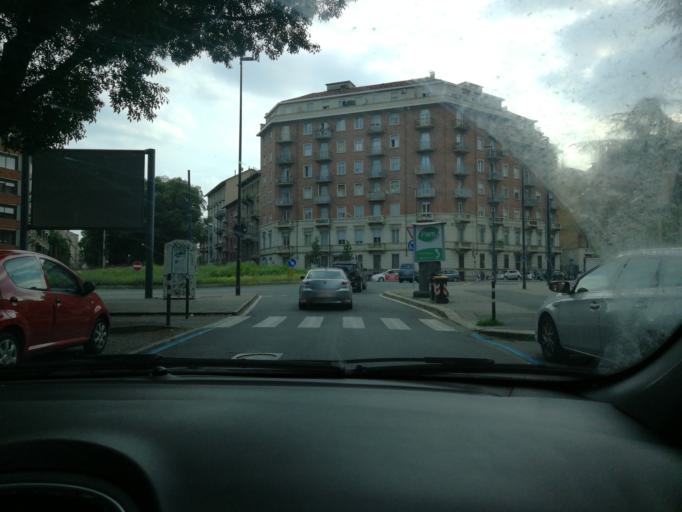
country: IT
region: Piedmont
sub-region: Provincia di Torino
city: Turin
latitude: 45.0835
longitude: 7.6516
